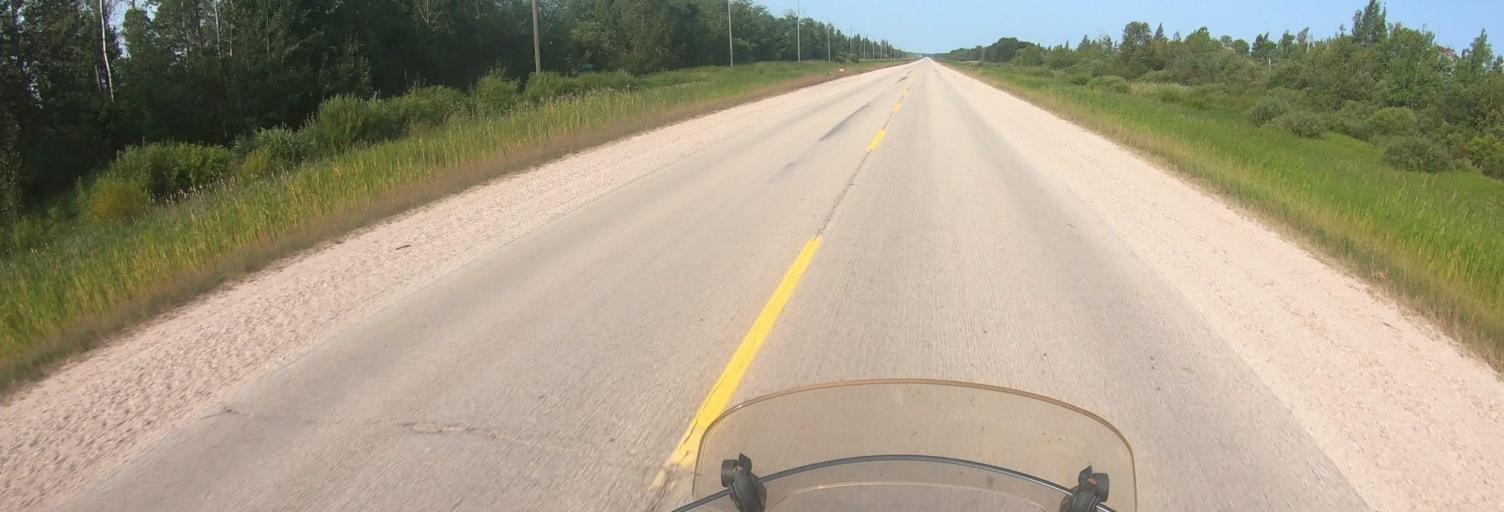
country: US
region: Minnesota
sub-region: Roseau County
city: Roseau
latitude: 49.0235
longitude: -95.6658
